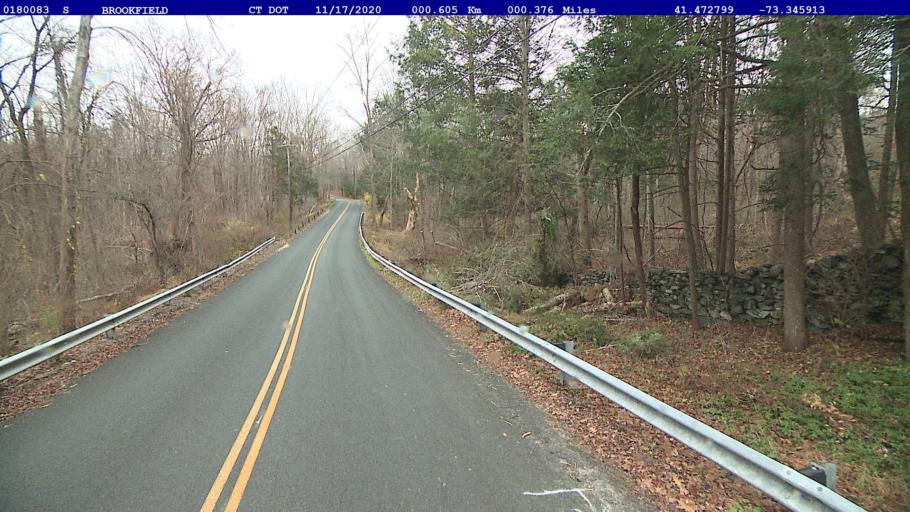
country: US
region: Connecticut
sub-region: Fairfield County
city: Newtown
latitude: 41.4728
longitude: -73.3458
